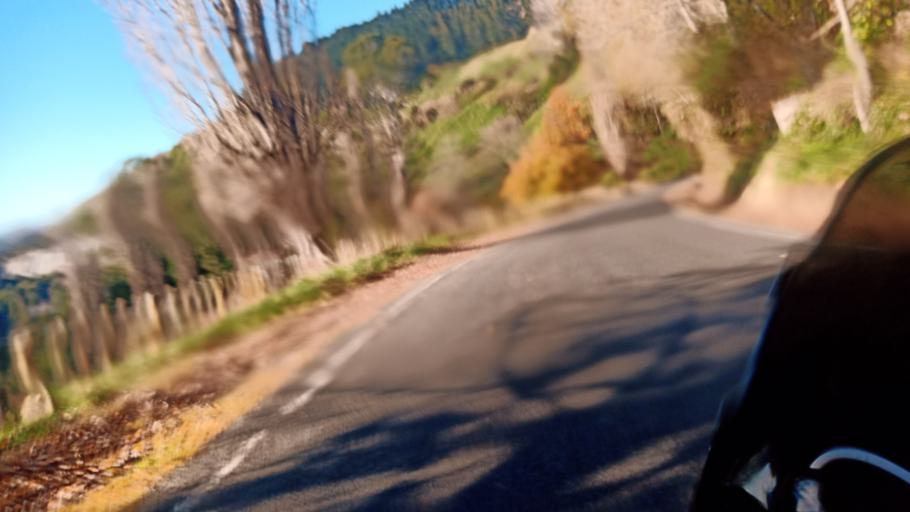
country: NZ
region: Hawke's Bay
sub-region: Wairoa District
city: Wairoa
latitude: -38.8197
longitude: 177.2946
